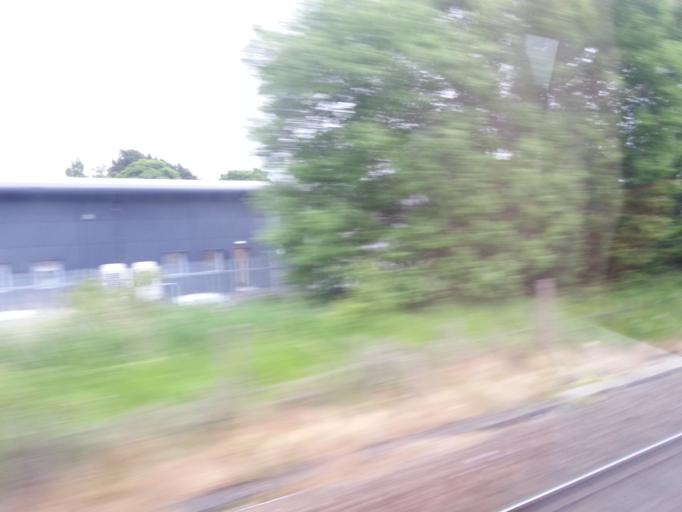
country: GB
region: Scotland
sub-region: Perth and Kinross
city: Perth
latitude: 56.4114
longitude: -3.4563
